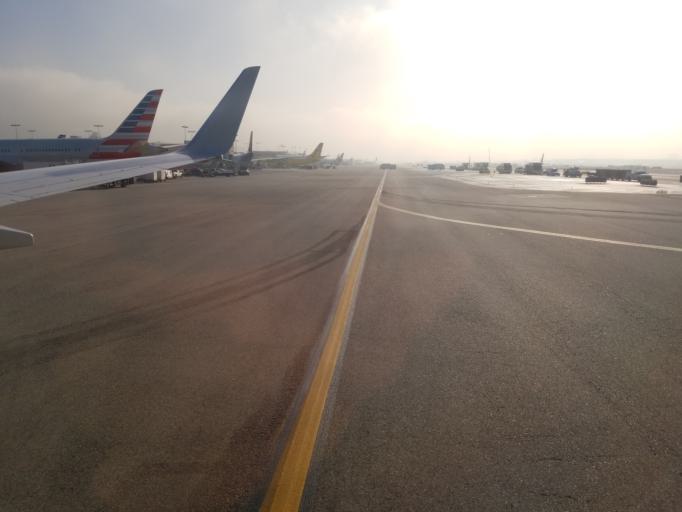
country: US
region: California
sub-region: Los Angeles County
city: El Segundo
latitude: 33.9388
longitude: -118.4075
